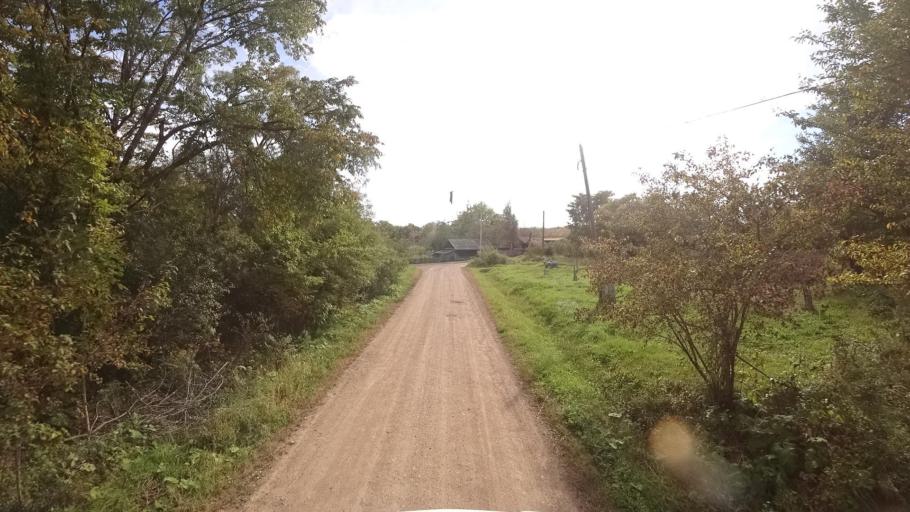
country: RU
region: Primorskiy
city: Dostoyevka
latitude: 44.2972
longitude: 133.4627
